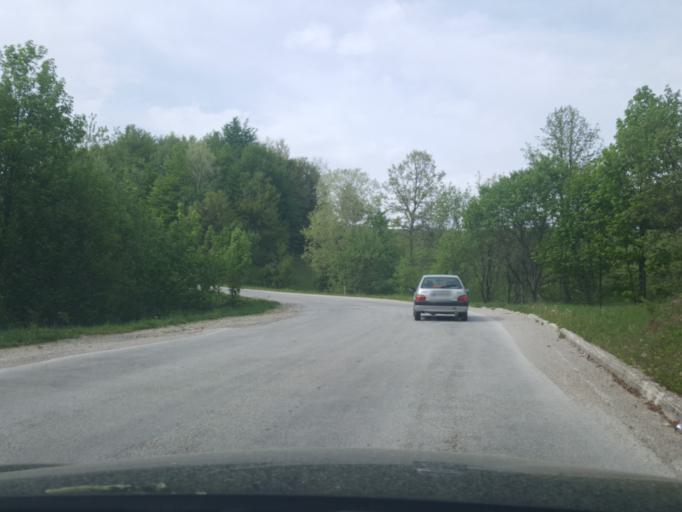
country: RS
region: Central Serbia
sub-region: Zlatiborski Okrug
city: Bajina Basta
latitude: 44.1053
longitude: 19.6663
